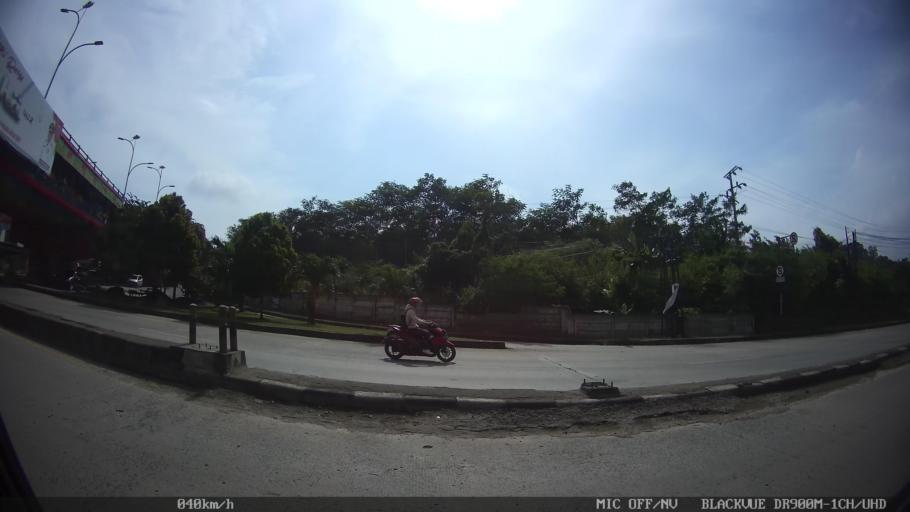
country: ID
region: Lampung
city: Kedaton
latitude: -5.3985
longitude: 105.2898
